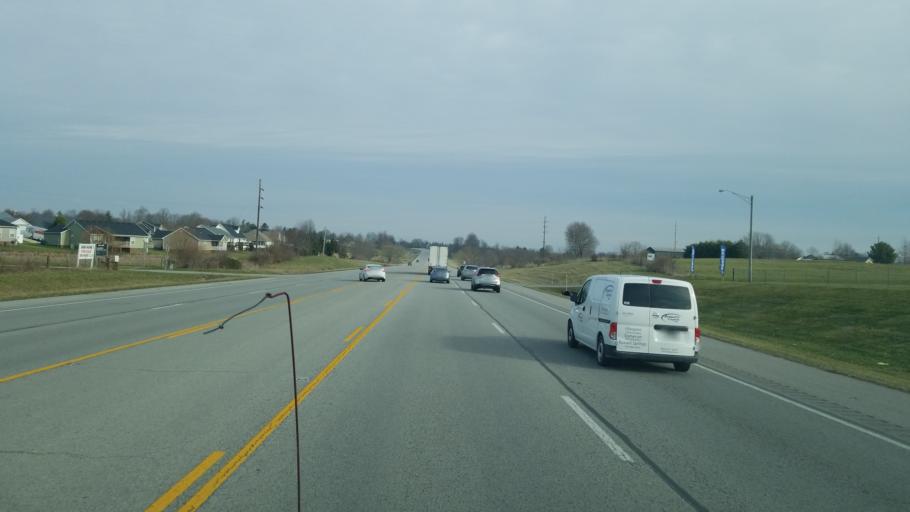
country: US
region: Kentucky
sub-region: Boyle County
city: Junction City
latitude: 37.5900
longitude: -84.7809
